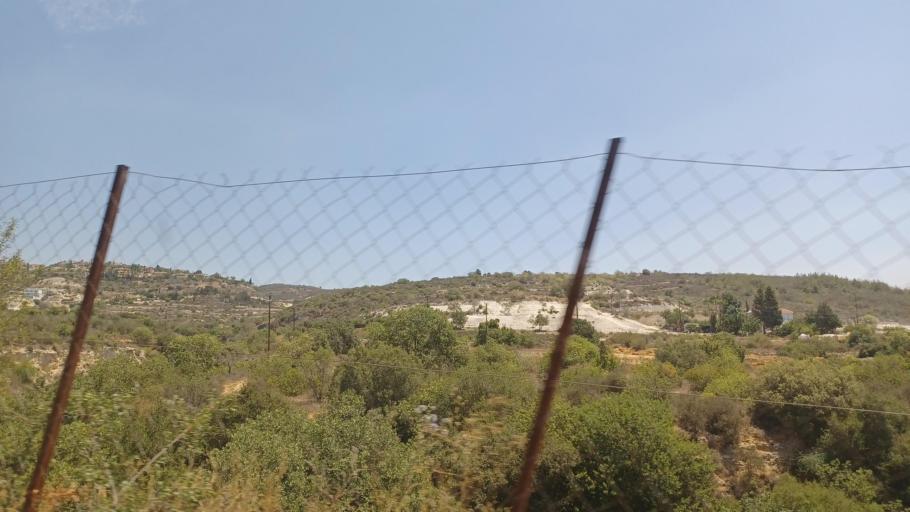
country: CY
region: Pafos
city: Mesogi
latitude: 34.8238
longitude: 32.4594
